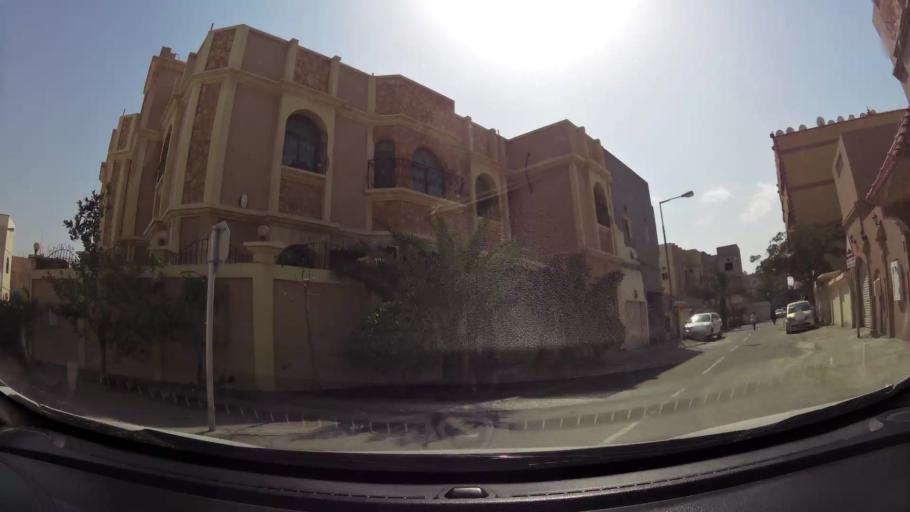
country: BH
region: Manama
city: Jidd Hafs
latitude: 26.2080
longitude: 50.4614
